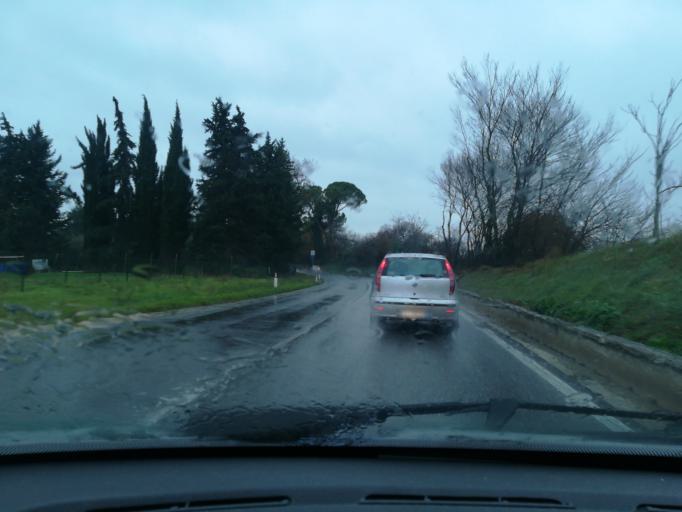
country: IT
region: The Marches
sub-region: Provincia di Macerata
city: Sforzacosta
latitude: 43.2730
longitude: 13.4276
